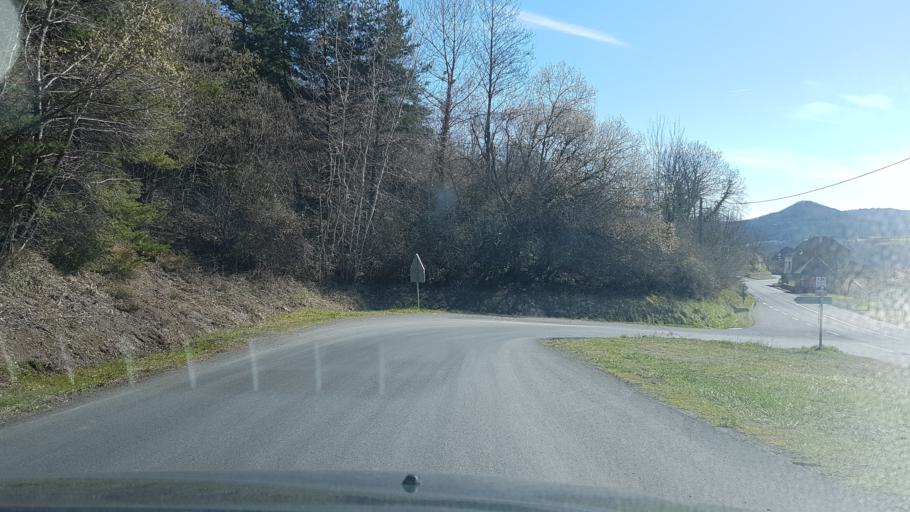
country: FR
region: Auvergne
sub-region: Departement du Puy-de-Dome
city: Aydat
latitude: 45.5457
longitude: 2.9989
